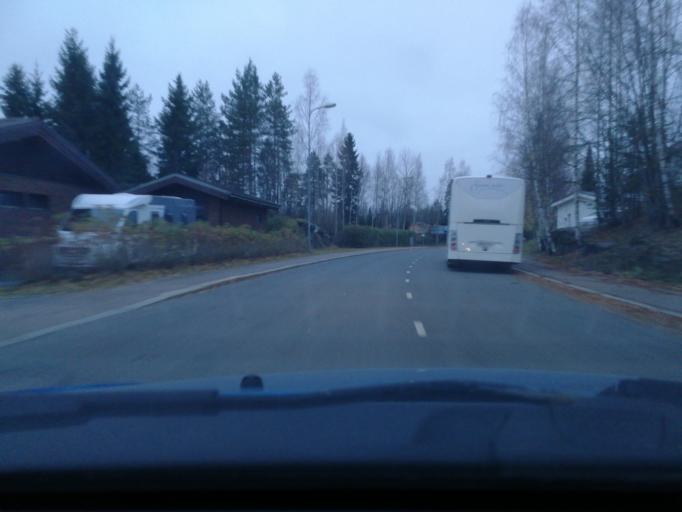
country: FI
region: Pirkanmaa
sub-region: Tampere
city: Tampere
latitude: 61.4440
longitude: 23.8728
